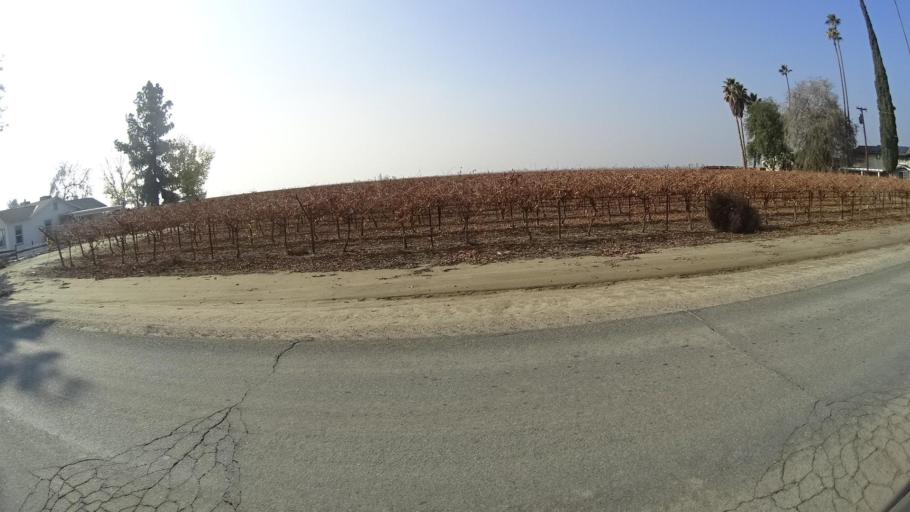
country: US
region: California
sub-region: Kern County
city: Greenfield
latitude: 35.2210
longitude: -119.0390
